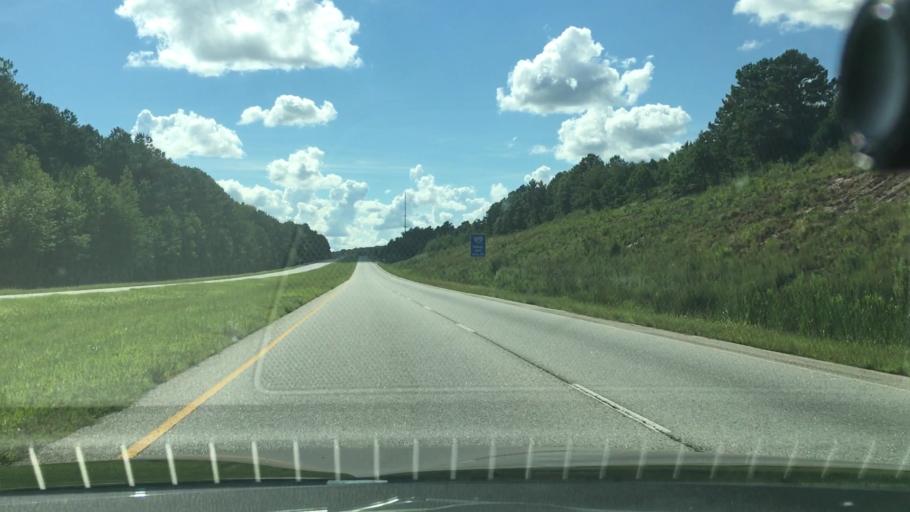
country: US
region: Georgia
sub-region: Spalding County
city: East Griffin
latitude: 33.2374
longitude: -84.1930
